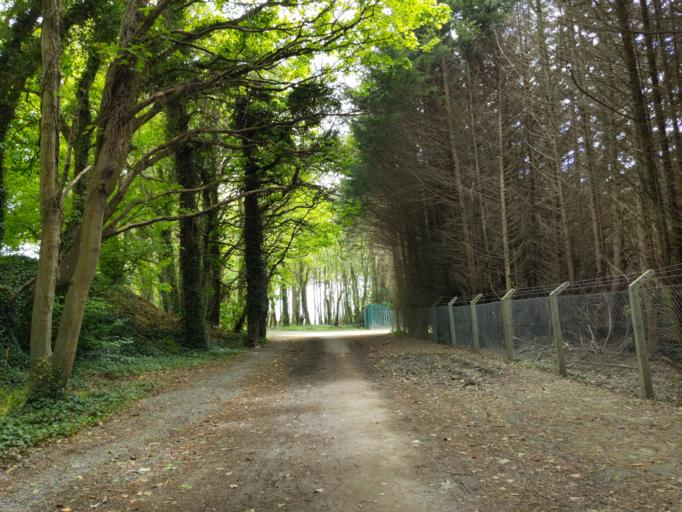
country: IE
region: Leinster
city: Portraine
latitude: 53.4866
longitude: -6.1167
